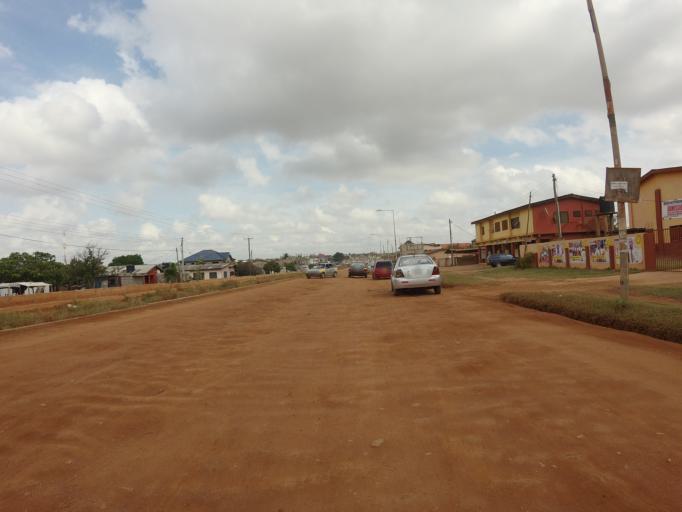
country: GH
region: Greater Accra
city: Teshi Old Town
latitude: 5.5995
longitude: -0.1195
